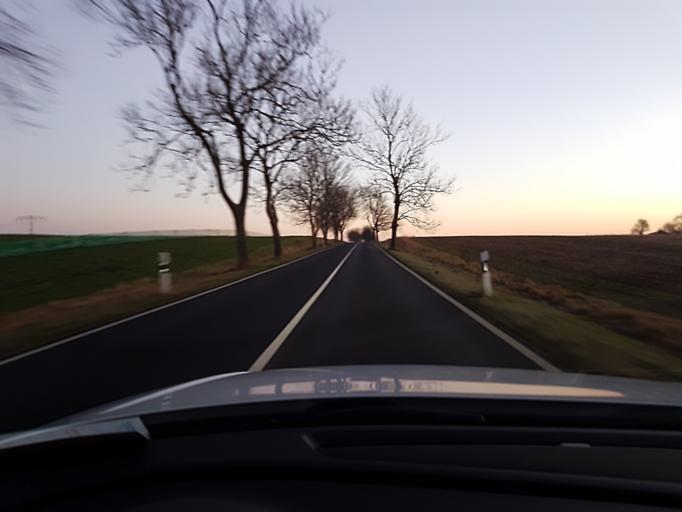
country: DE
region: Mecklenburg-Vorpommern
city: Gingst
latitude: 54.4997
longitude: 13.2800
